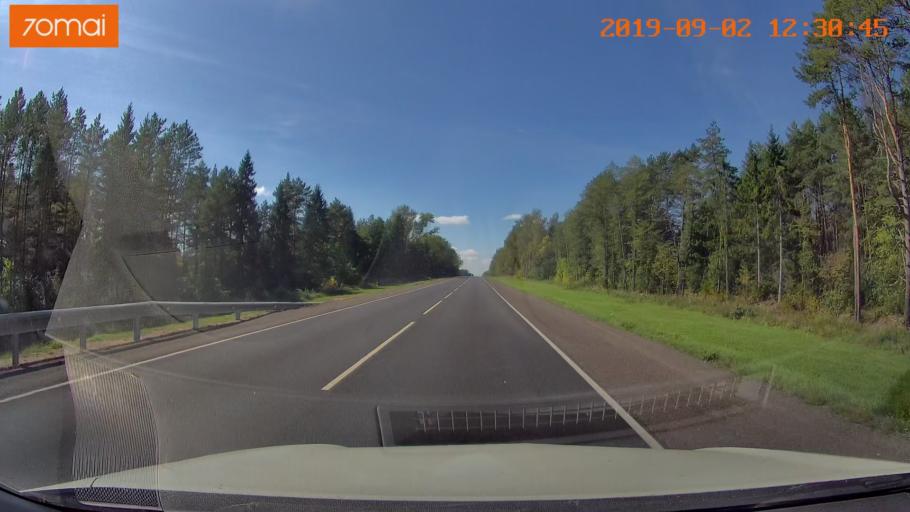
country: RU
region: Smolensk
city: Shumyachi
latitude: 53.8297
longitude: 32.4669
